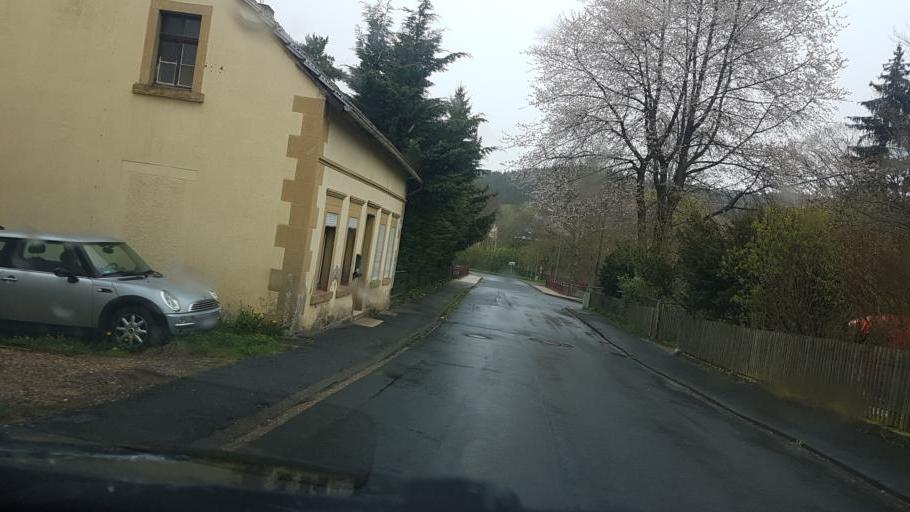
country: DE
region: Rheinland-Pfalz
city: Junkerath
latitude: 50.3397
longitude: 6.5859
